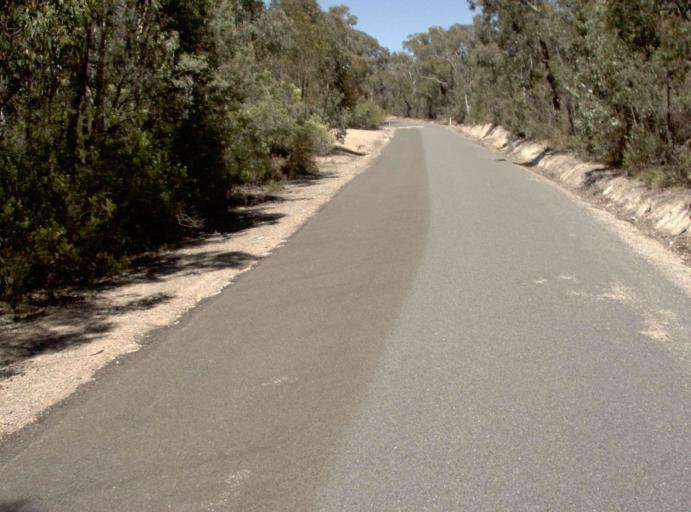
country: AU
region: New South Wales
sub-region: Snowy River
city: Jindabyne
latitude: -37.1239
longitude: 148.2489
